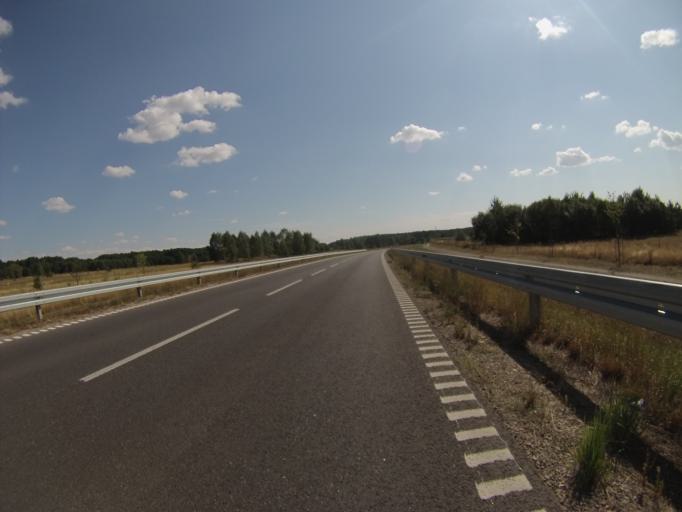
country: PL
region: Swietokrzyskie
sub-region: Powiat kielecki
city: Rakow
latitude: 50.6829
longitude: 21.0461
